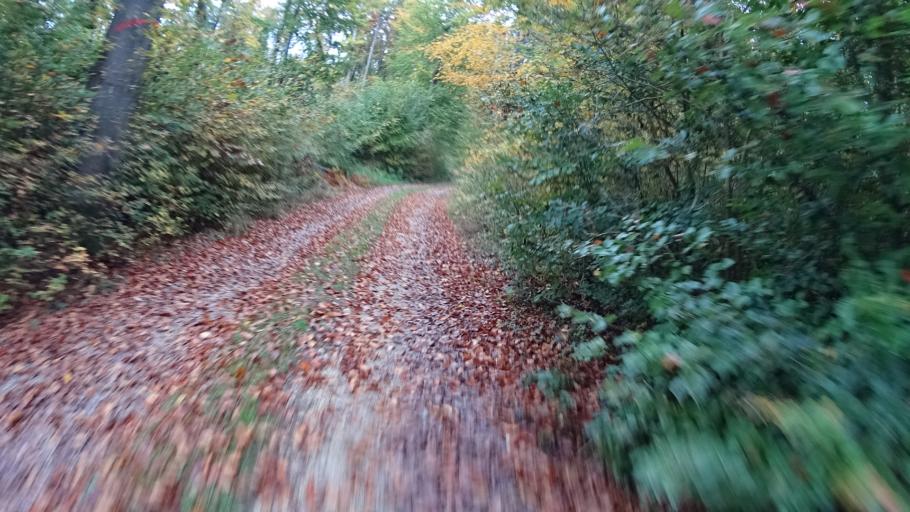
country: DE
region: Bavaria
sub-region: Upper Bavaria
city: Adelschlag
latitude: 48.8680
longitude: 11.2530
